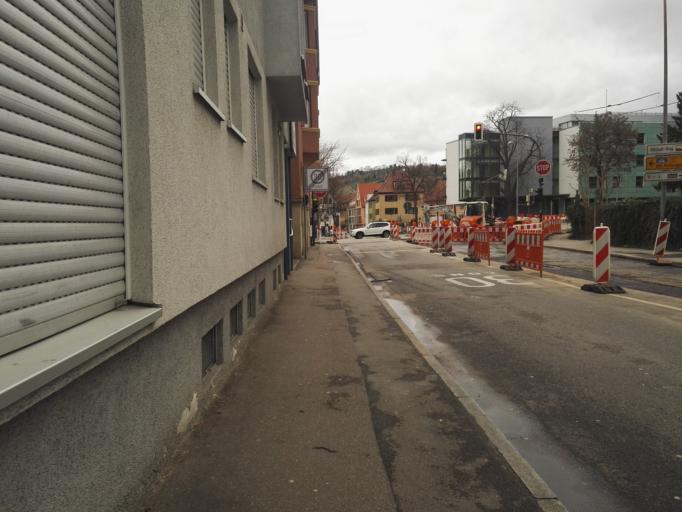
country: DE
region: Baden-Wuerttemberg
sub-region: Regierungsbezirk Stuttgart
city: Esslingen
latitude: 48.7410
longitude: 9.3147
